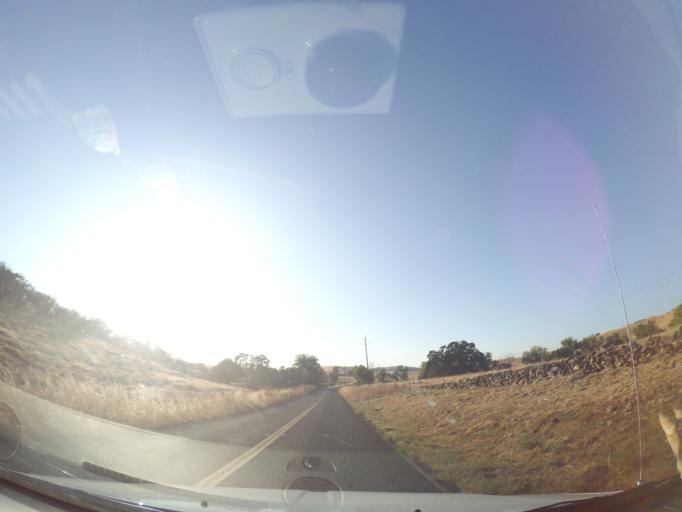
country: US
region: California
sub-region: Merced County
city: Planada
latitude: 37.4968
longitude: -120.2315
